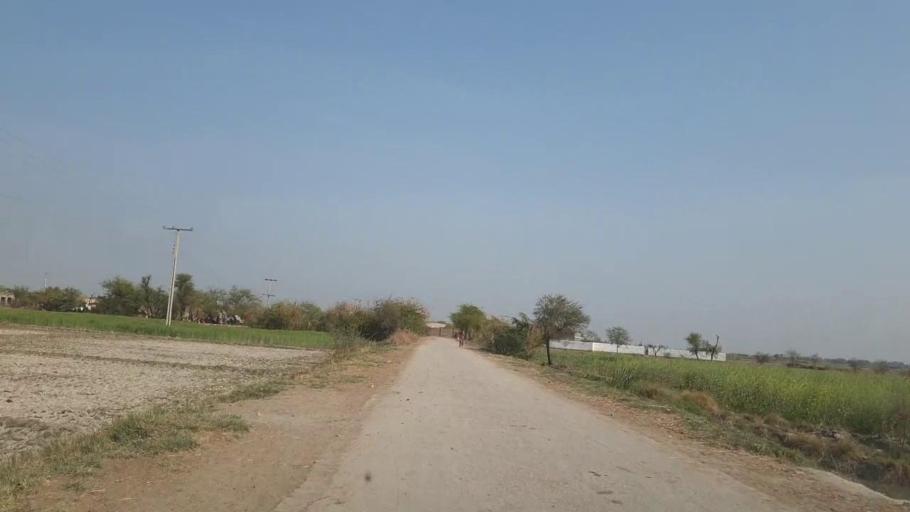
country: PK
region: Sindh
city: Pithoro
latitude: 25.7233
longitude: 69.2215
